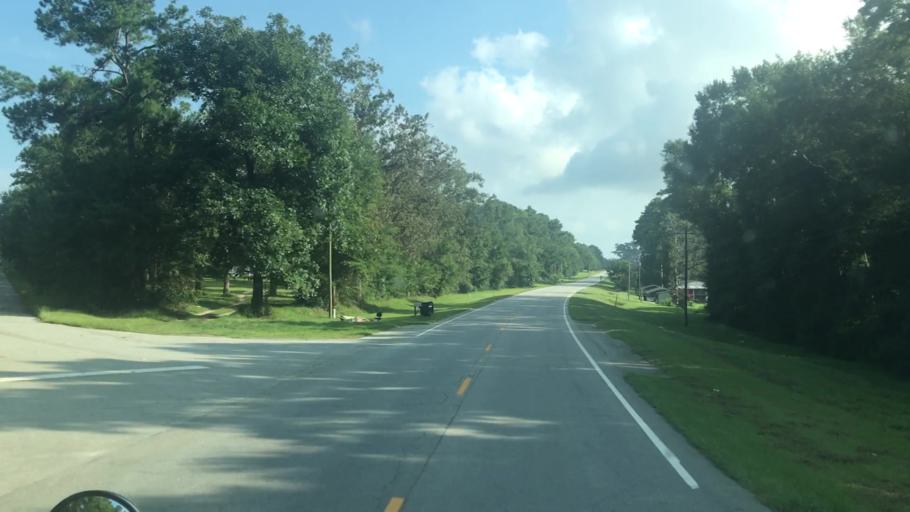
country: US
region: Florida
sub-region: Gadsden County
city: Havana
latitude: 30.7531
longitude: -84.4879
